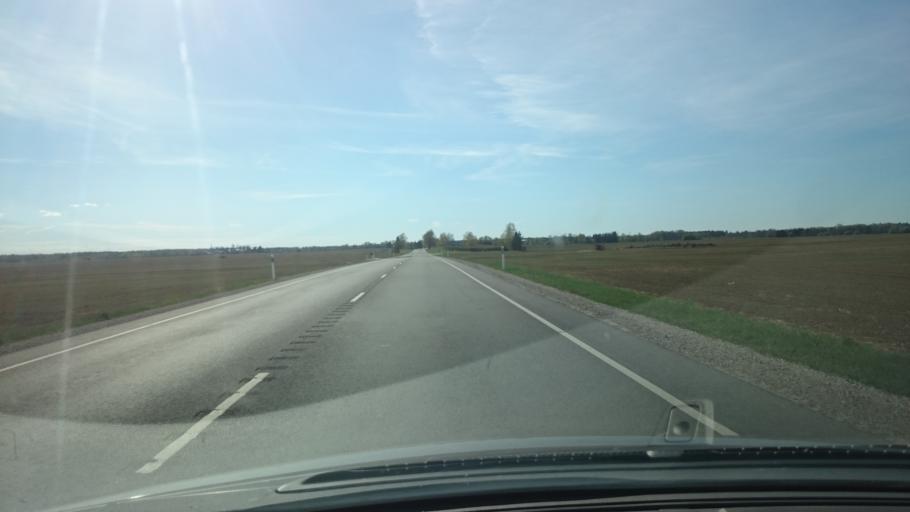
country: EE
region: Laeaene-Virumaa
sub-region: Haljala vald
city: Haljala
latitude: 59.3490
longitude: 26.2519
